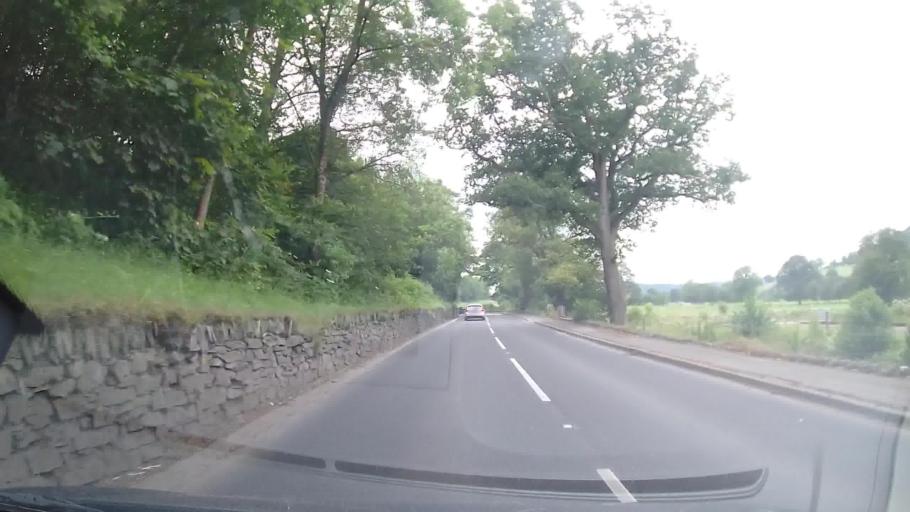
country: GB
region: Wales
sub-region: Denbighshire
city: Corwen
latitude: 52.9810
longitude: -3.3506
